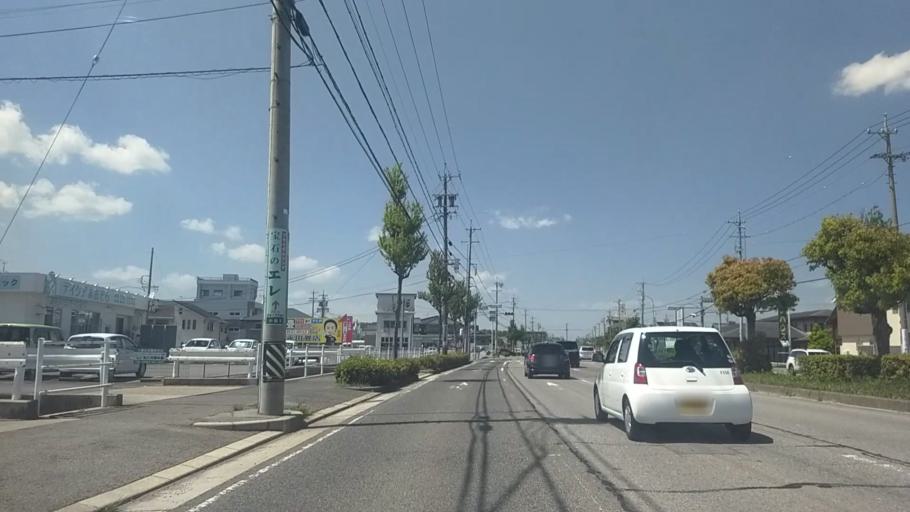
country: JP
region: Aichi
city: Okazaki
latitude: 34.9629
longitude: 137.1850
